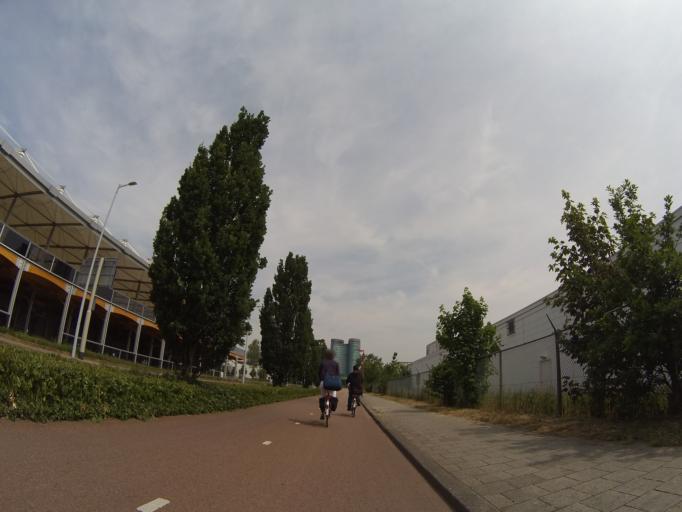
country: NL
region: Utrecht
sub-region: Gemeente Utrecht
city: Utrecht
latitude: 52.0803
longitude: 5.1037
